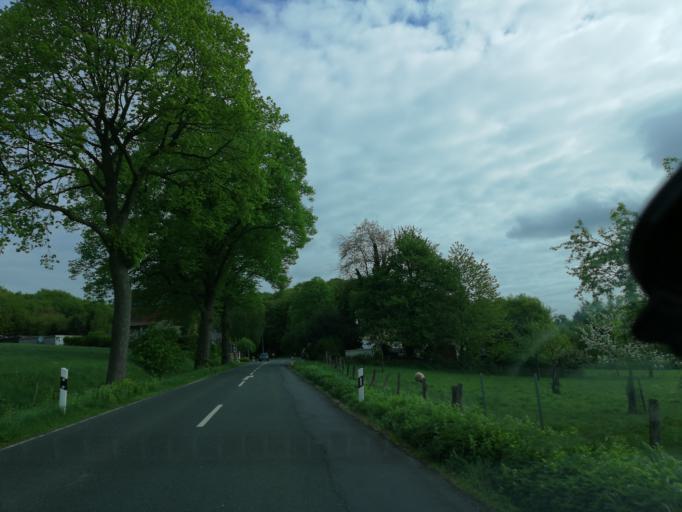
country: DE
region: North Rhine-Westphalia
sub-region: Regierungsbezirk Arnsberg
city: Schwelm
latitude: 51.3098
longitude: 7.2843
